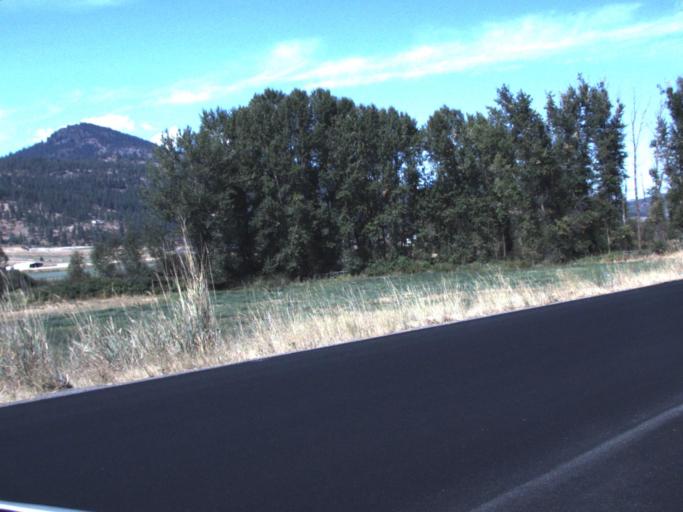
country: US
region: Washington
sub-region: Stevens County
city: Colville
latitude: 48.4848
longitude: -117.9023
